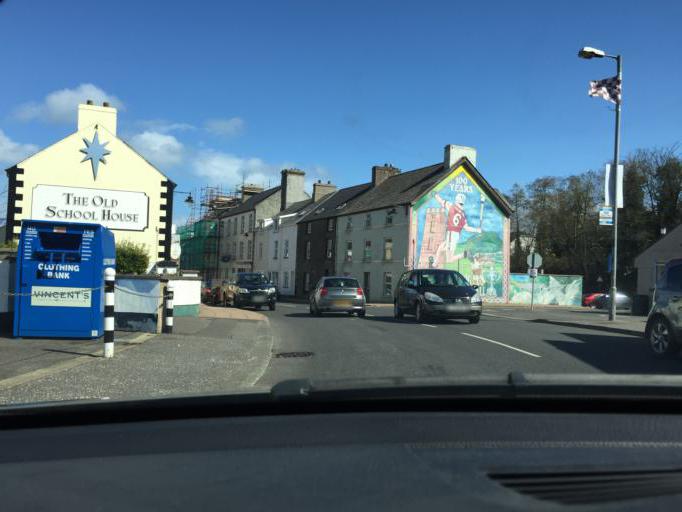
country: GB
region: Northern Ireland
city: Cushendall
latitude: 55.0798
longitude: -6.0657
